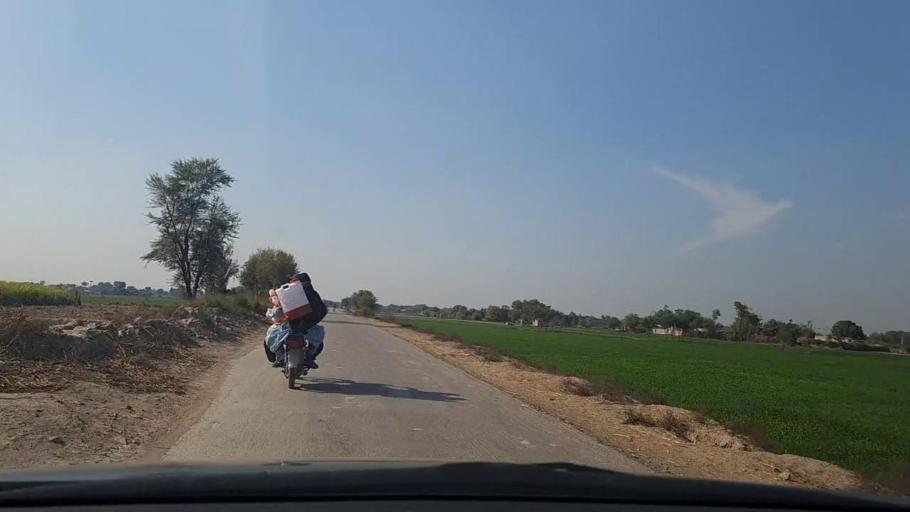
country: PK
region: Sindh
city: Daulatpur
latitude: 26.3127
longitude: 68.0723
